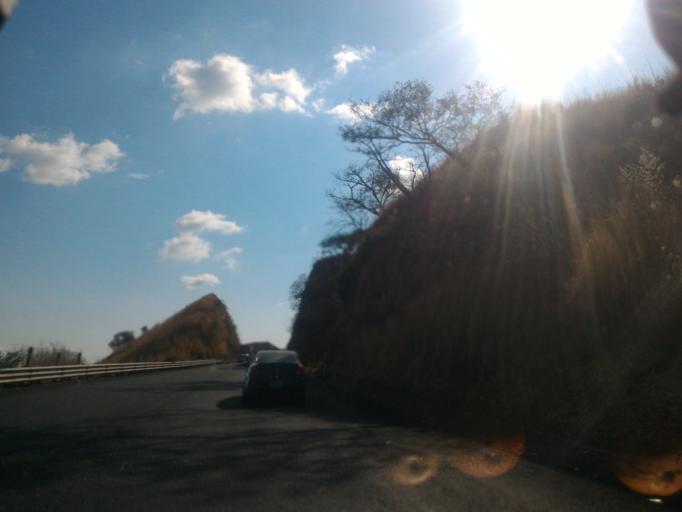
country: MX
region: Jalisco
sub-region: Tonila
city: San Marcos
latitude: 19.4566
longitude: -103.4669
